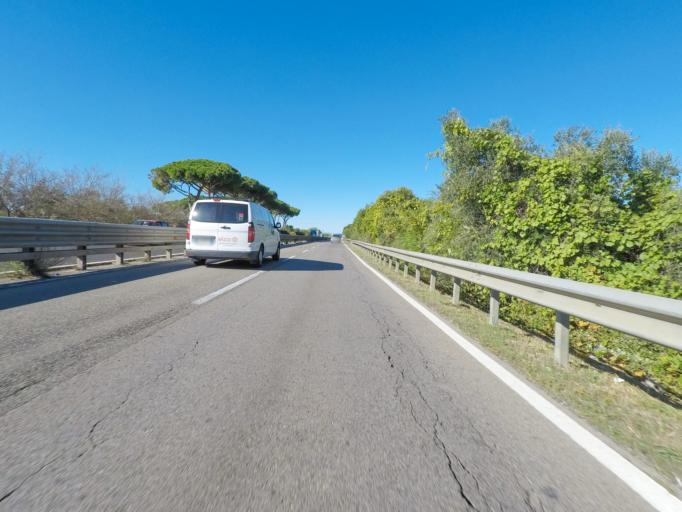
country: IT
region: Tuscany
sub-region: Provincia di Grosseto
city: Grosseto
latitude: 42.7229
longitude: 11.1381
